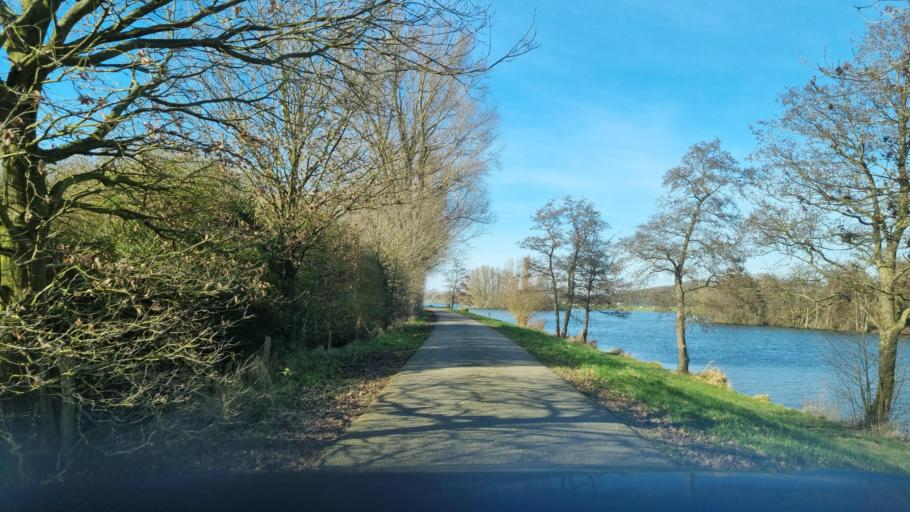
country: NL
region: North Brabant
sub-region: Gemeente Cuijk
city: Cuijk
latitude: 51.7363
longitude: 5.9057
